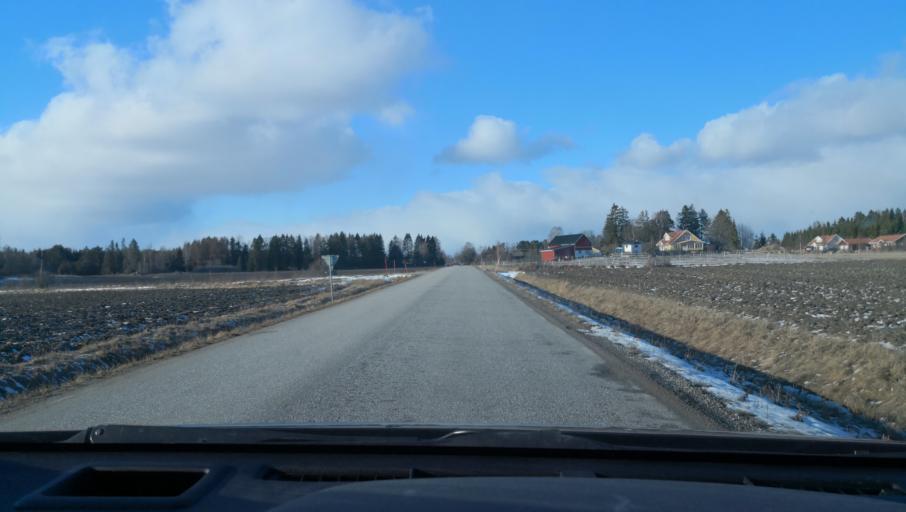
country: SE
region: Uppsala
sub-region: Enkopings Kommun
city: Hummelsta
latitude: 59.6315
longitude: 16.9764
